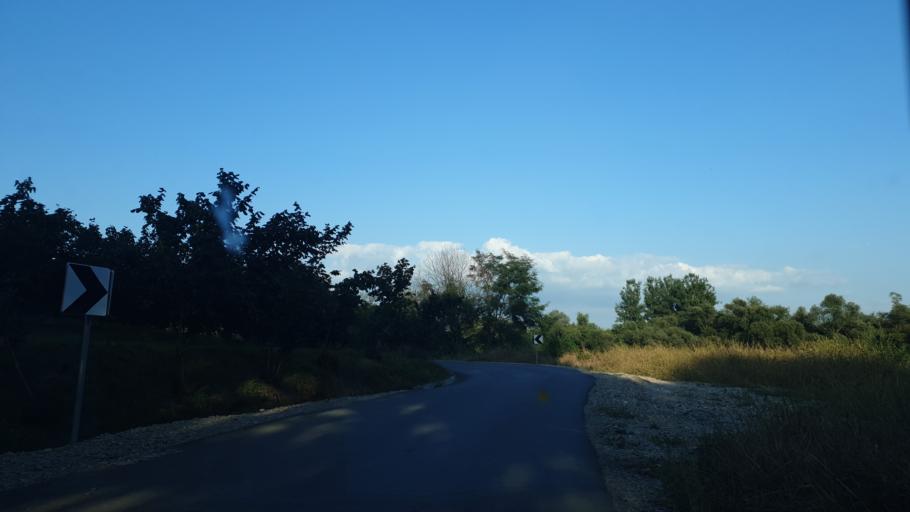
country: RS
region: Central Serbia
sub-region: Zlatiborski Okrug
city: Pozega
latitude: 43.8656
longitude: 19.9908
